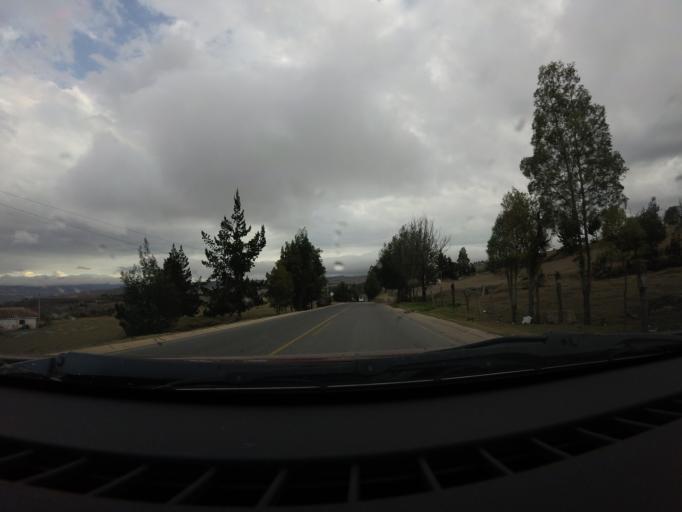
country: CO
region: Boyaca
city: Tunja
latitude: 5.5541
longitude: -73.4076
